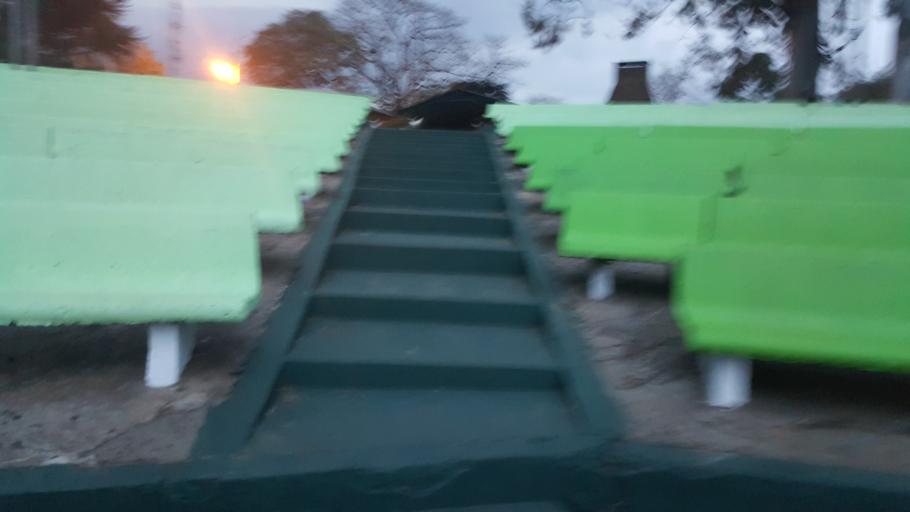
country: AR
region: Corrientes
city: Ituzaingo
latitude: -27.5852
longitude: -56.6916
